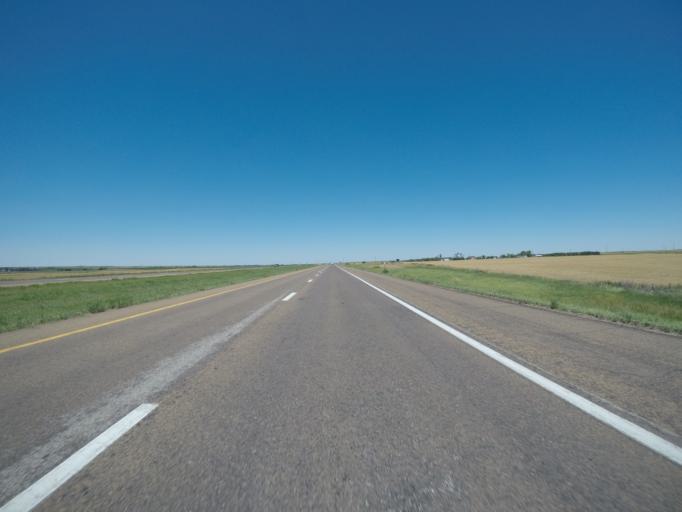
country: US
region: Kansas
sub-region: Ellis County
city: Hays
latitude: 38.9259
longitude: -99.4382
